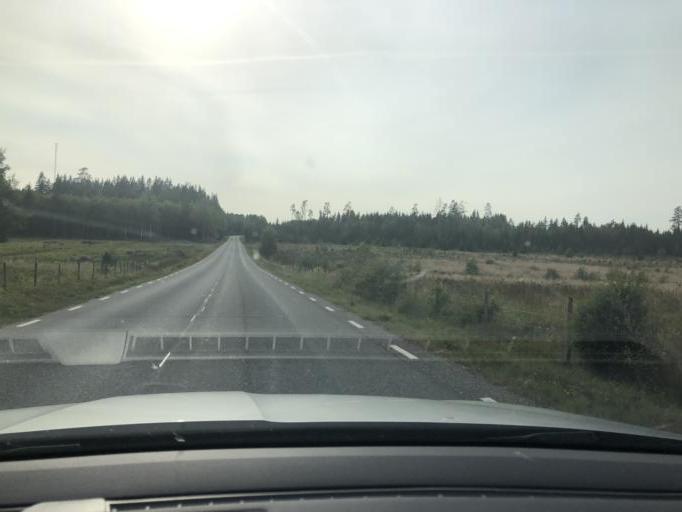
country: SE
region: Joenkoeping
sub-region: Vetlanda Kommun
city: Ekenassjon
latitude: 57.5274
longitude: 14.9309
